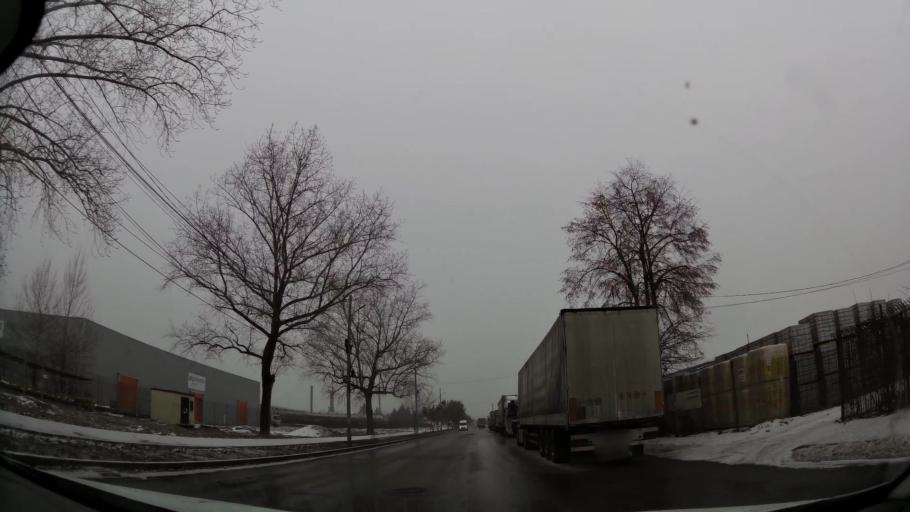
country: RO
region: Dambovita
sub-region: Municipiul Targoviste
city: Targoviste
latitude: 44.9192
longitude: 25.4366
